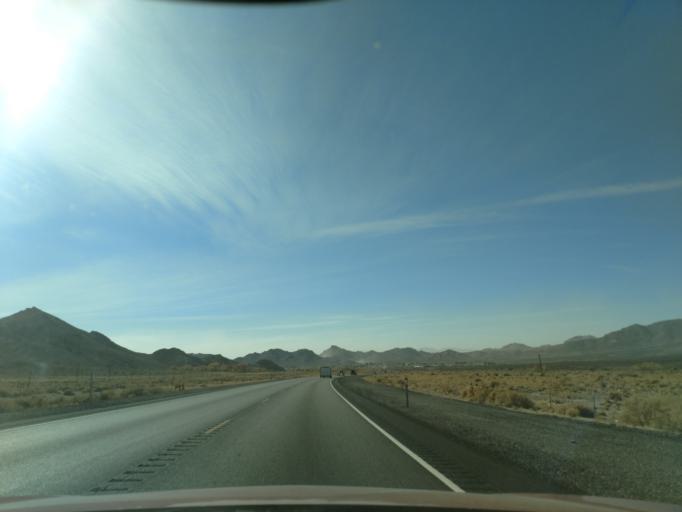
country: US
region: Nevada
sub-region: Nye County
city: Beatty
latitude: 36.9255
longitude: -116.7383
